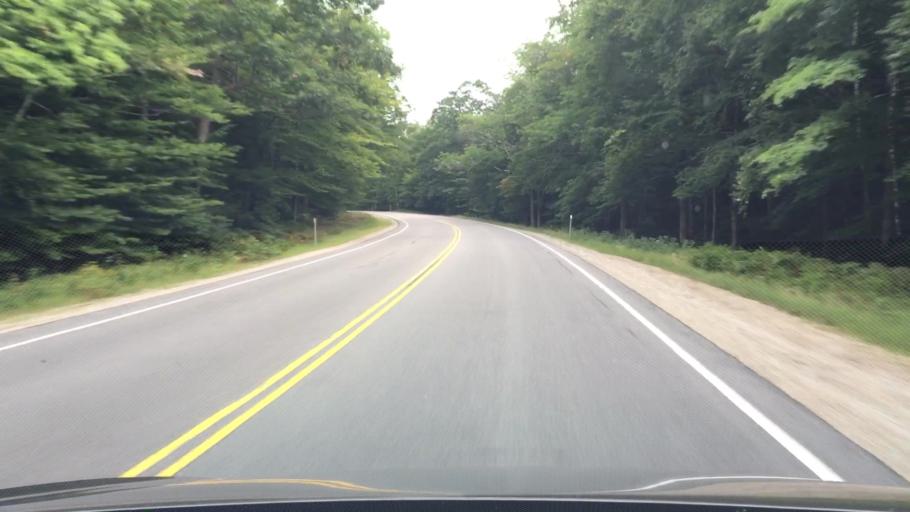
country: US
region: New Hampshire
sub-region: Carroll County
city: Conway
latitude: 44.0025
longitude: -71.2399
